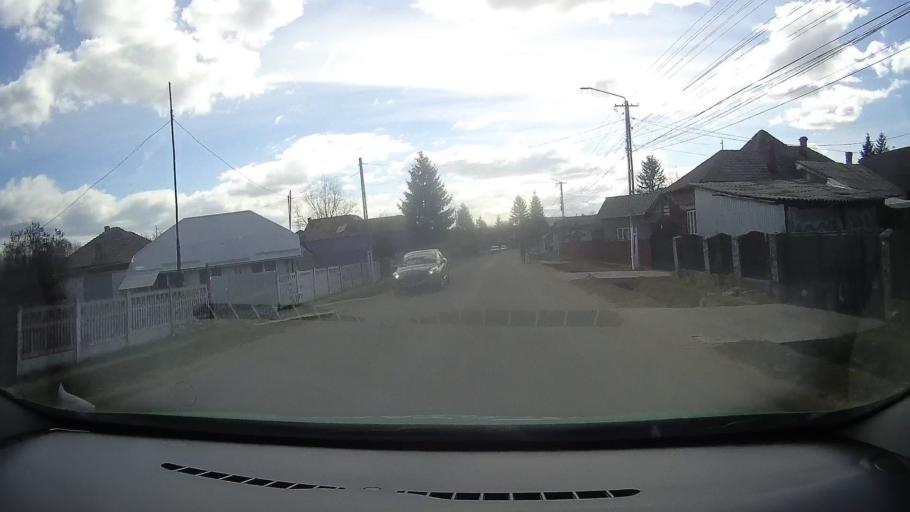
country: RO
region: Dambovita
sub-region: Comuna Doicesti
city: Doicesti
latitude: 44.9761
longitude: 25.3922
